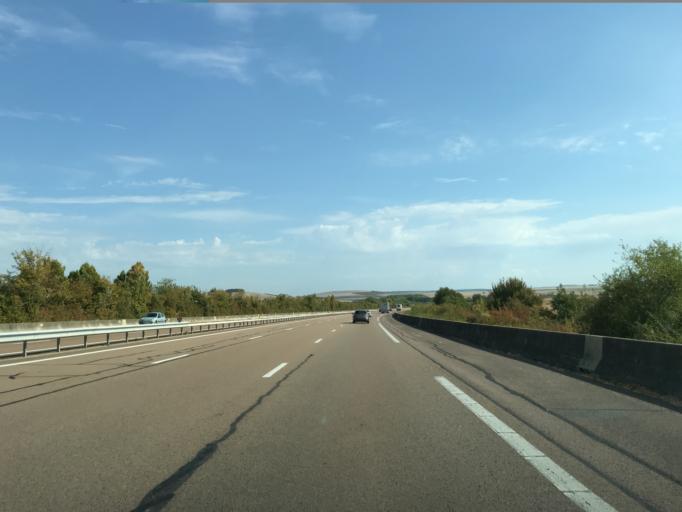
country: FR
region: Bourgogne
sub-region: Departement de l'Yonne
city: Aillant-sur-Tholon
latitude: 47.9102
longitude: 3.3328
